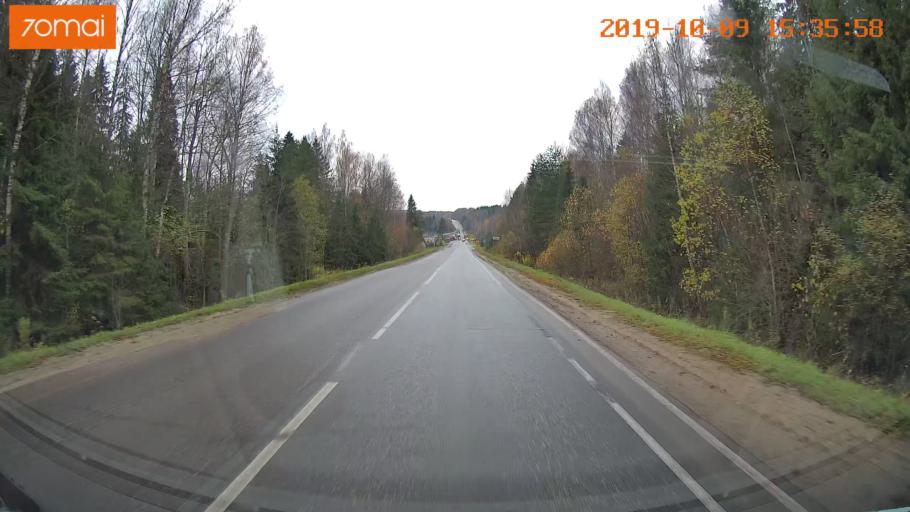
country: RU
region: Kostroma
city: Oktyabr'skiy
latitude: 57.9270
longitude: 41.2171
